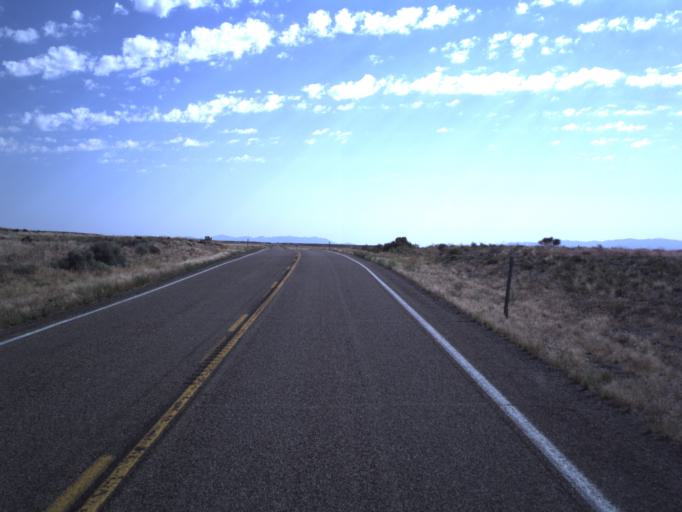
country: US
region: Utah
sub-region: Beaver County
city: Milford
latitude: 38.8138
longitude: -112.8661
